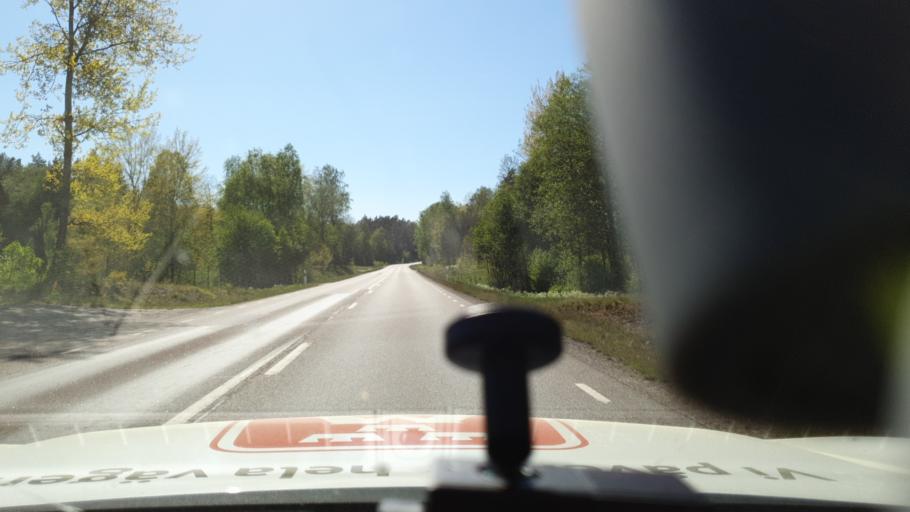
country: SE
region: Kalmar
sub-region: Hultsfreds Kommun
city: Virserum
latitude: 57.4065
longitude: 15.5575
